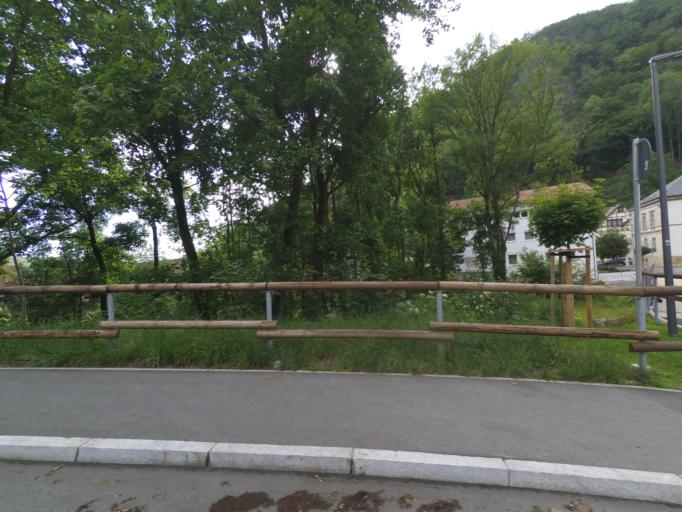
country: DE
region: Bavaria
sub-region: Upper Franconia
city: Bad Berneck im Fichtelgebirge
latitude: 50.0453
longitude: 11.6709
